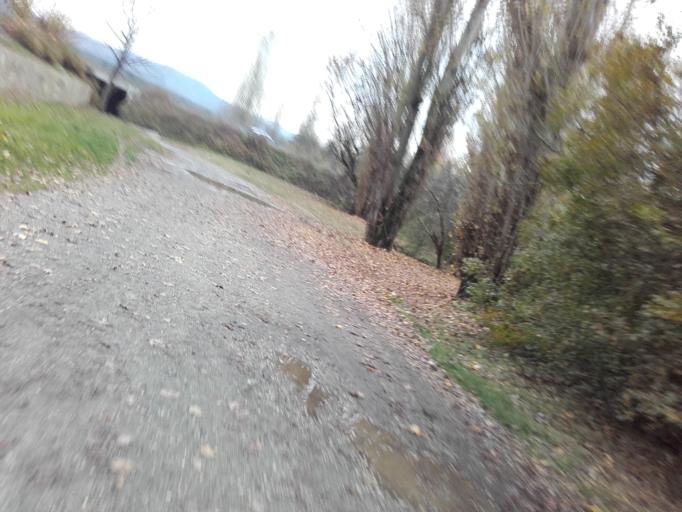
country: IT
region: Piedmont
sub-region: Provincia di Torino
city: Settimo Torinese
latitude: 45.1243
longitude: 7.7666
